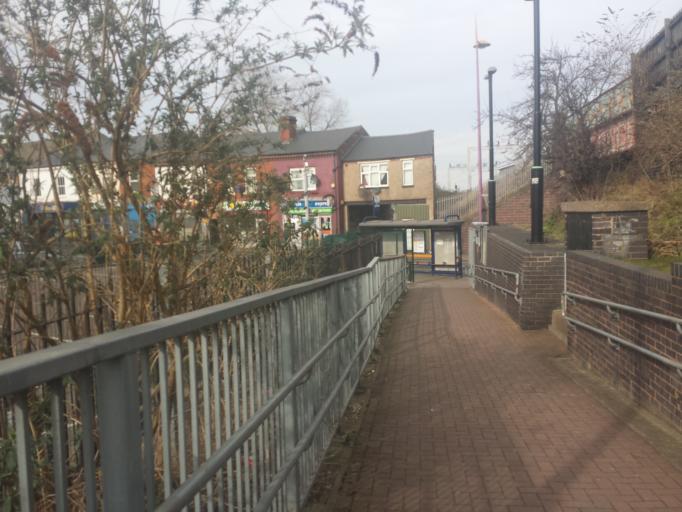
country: GB
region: England
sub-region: City and Borough of Birmingham
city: Hockley
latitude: 52.5125
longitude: -1.8847
